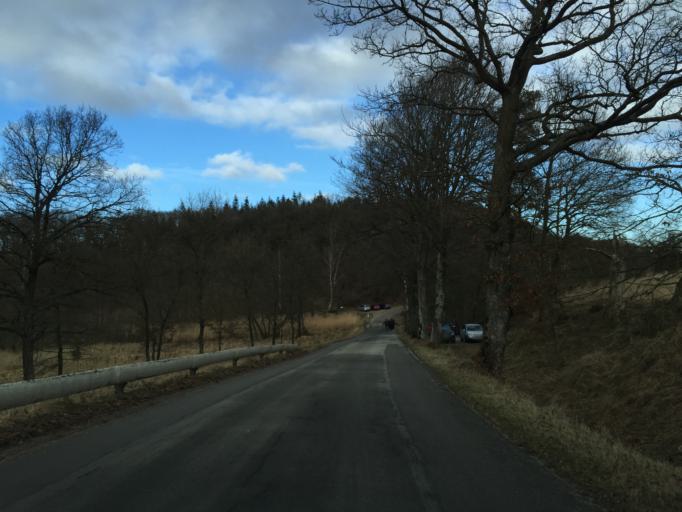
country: DK
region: Central Jutland
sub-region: Viborg Kommune
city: Viborg
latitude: 56.3804
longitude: 9.3313
